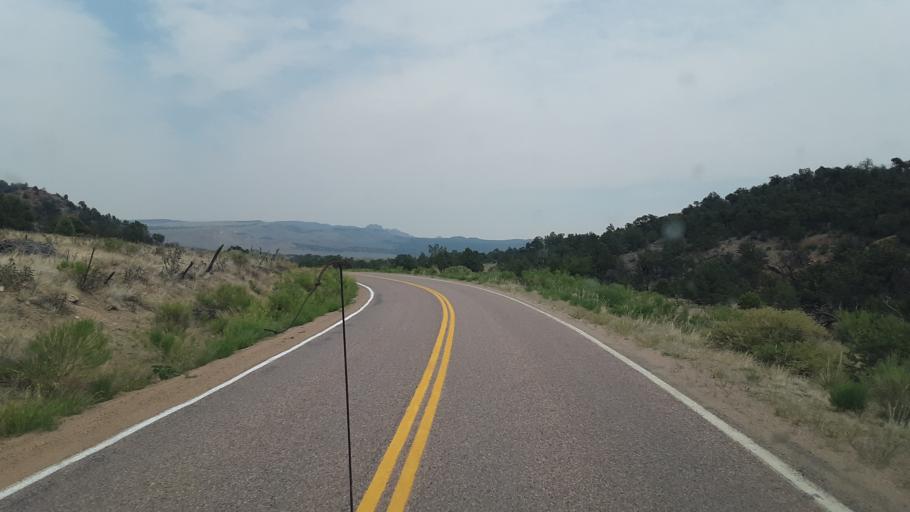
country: US
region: Colorado
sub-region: Fremont County
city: Canon City
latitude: 38.4322
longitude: -105.3881
